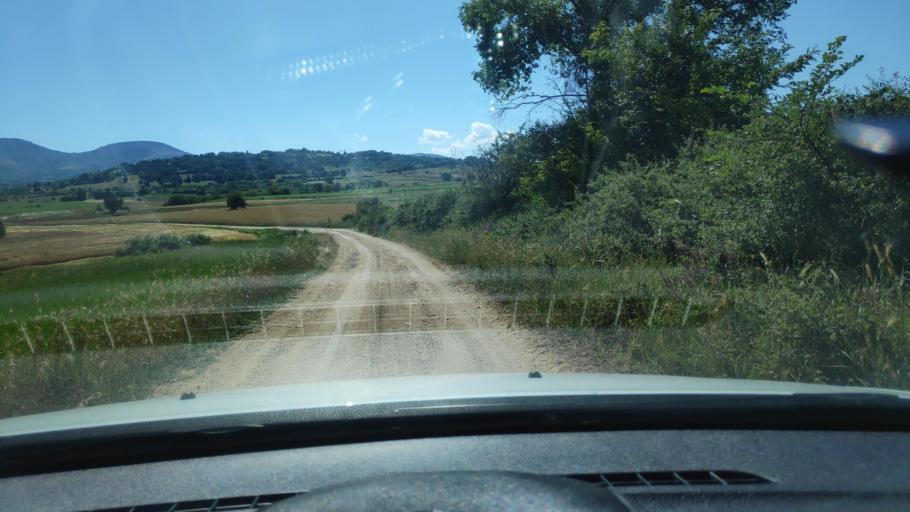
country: MK
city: Klechovce
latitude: 42.0674
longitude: 21.8612
